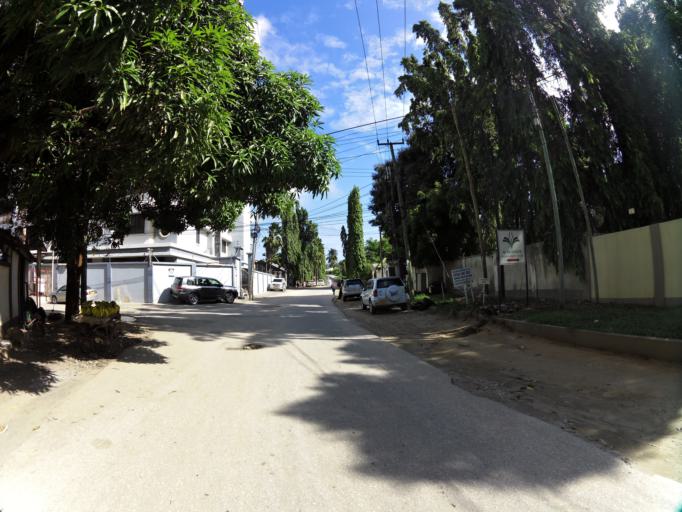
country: TZ
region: Dar es Salaam
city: Dar es Salaam
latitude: -6.8011
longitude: 39.2745
